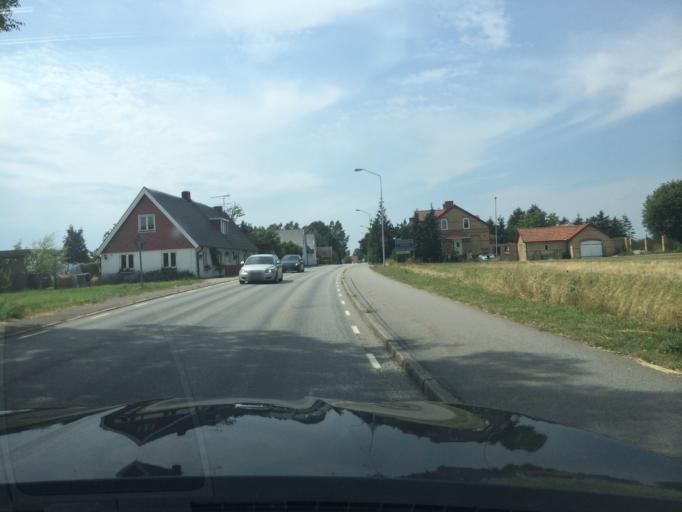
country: SE
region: Skane
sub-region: Kavlinge Kommun
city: Loddekopinge
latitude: 55.7676
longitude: 13.0526
